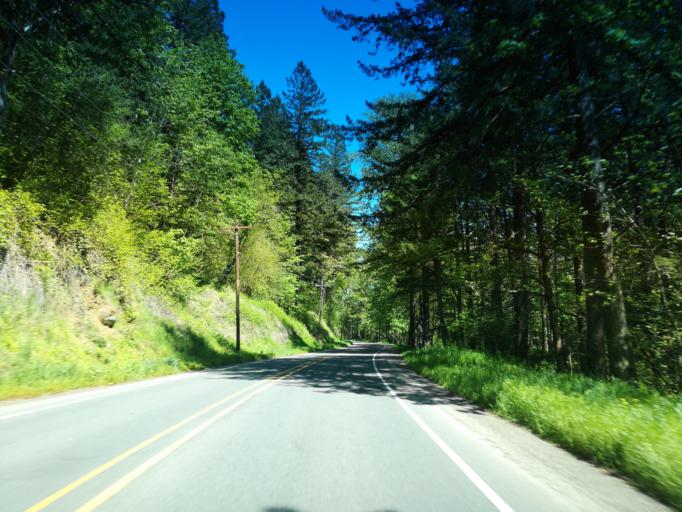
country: US
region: Oregon
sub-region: Multnomah County
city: Troutdale
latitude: 45.5178
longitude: -122.3562
